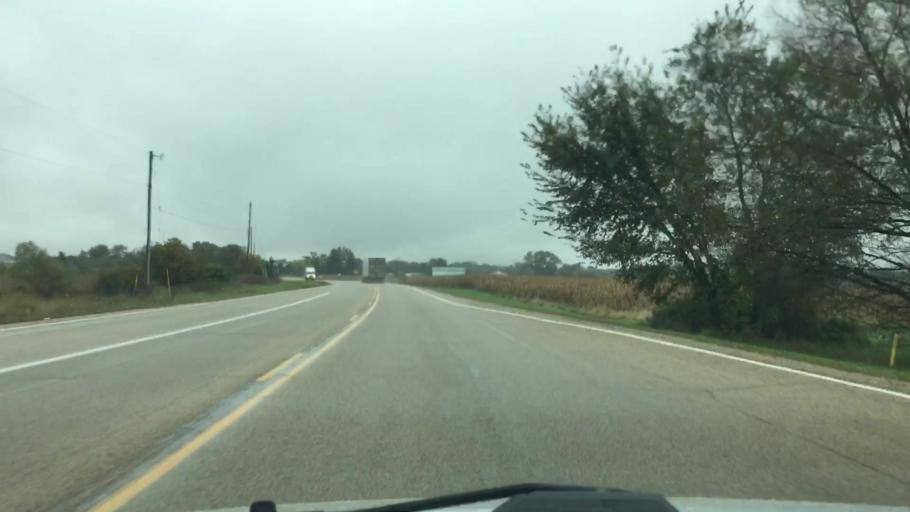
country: US
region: Wisconsin
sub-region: Walworth County
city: Whitewater
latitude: 42.8477
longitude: -88.7188
